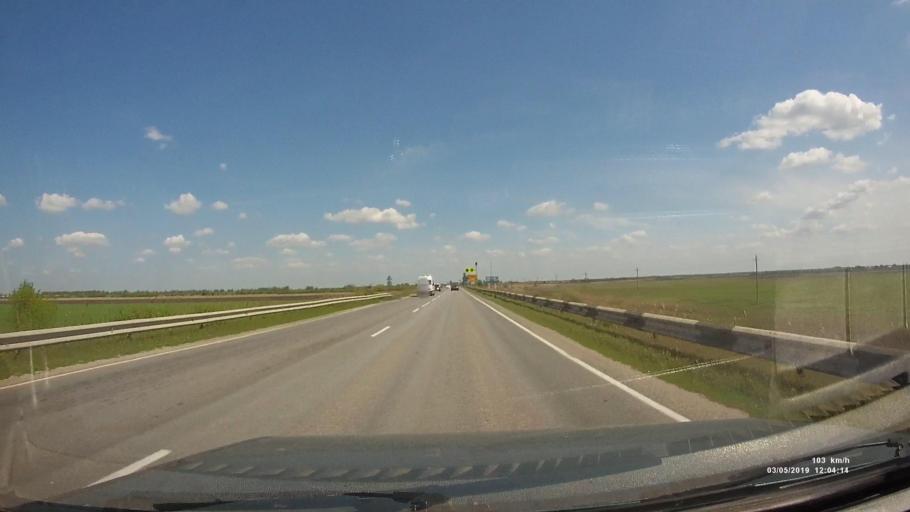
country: RU
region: Rostov
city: Bagayevskaya
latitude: 47.2772
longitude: 40.4070
